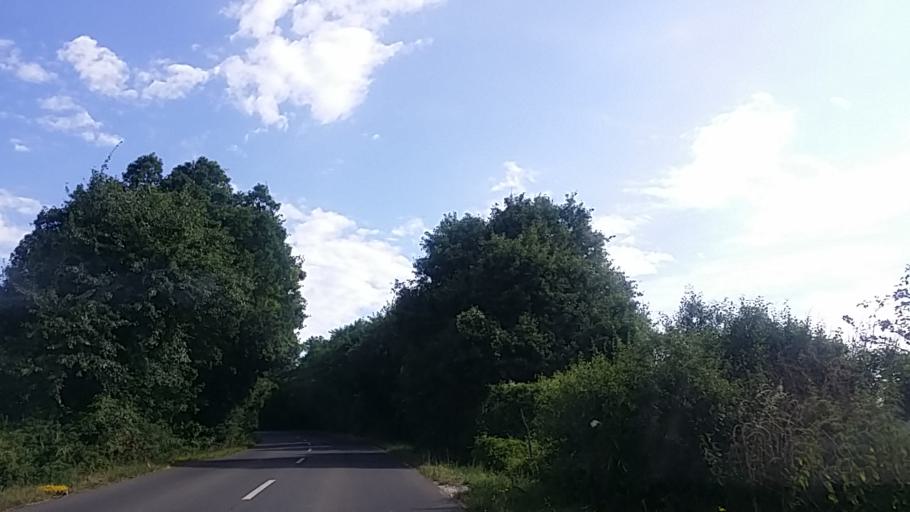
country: HU
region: Nograd
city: Romhany
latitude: 47.8517
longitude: 19.2599
